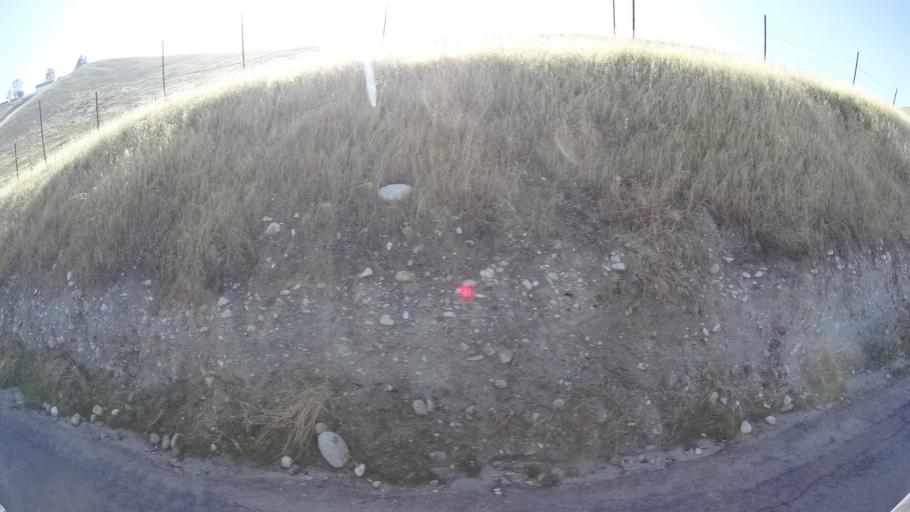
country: US
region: California
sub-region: Kern County
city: Lamont
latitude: 35.3907
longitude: -118.8165
